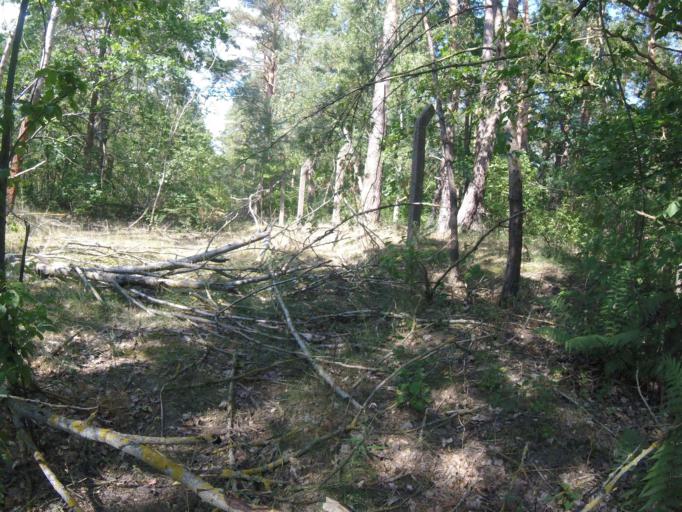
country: DE
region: Brandenburg
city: Wildau
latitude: 52.3288
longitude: 13.6682
